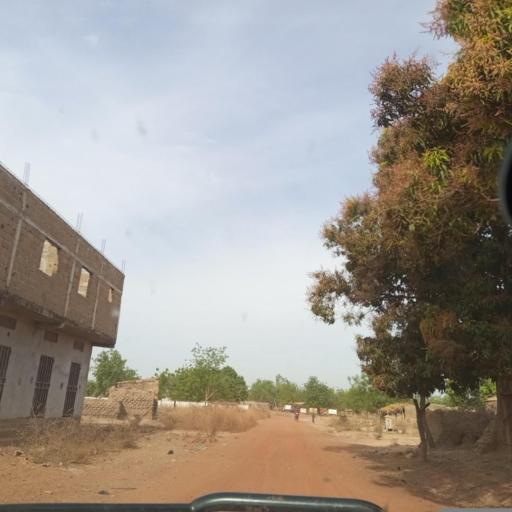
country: ML
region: Koulikoro
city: Koulikoro
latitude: 13.1110
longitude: -7.6520
